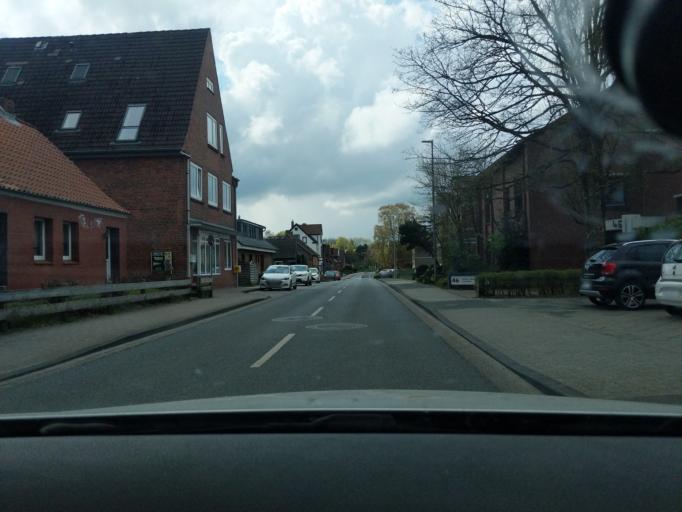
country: DE
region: Lower Saxony
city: Stade
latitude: 53.5898
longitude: 9.4674
